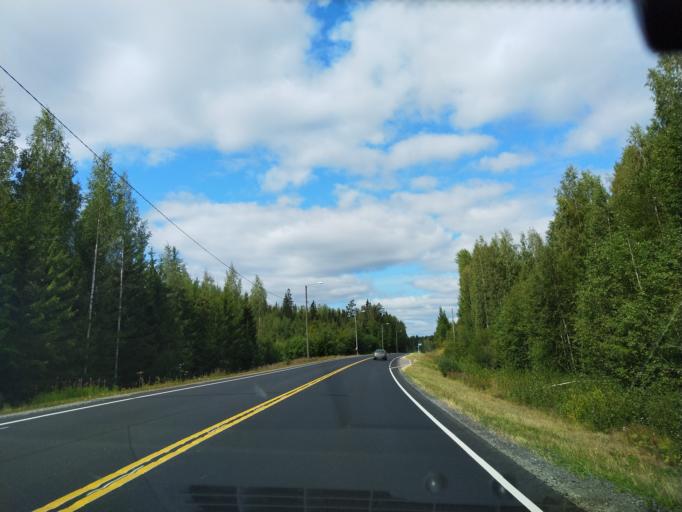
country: FI
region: Haeme
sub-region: Riihimaeki
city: Loppi
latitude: 60.7153
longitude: 24.4692
